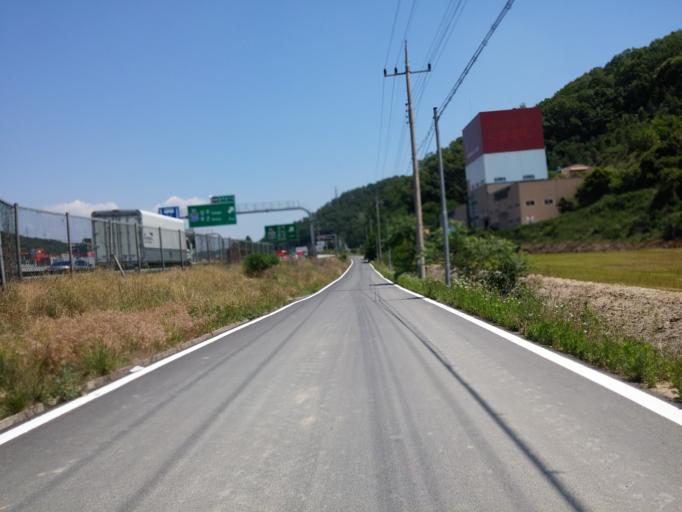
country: KR
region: Daejeon
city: Sintansin
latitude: 36.5435
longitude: 127.4321
